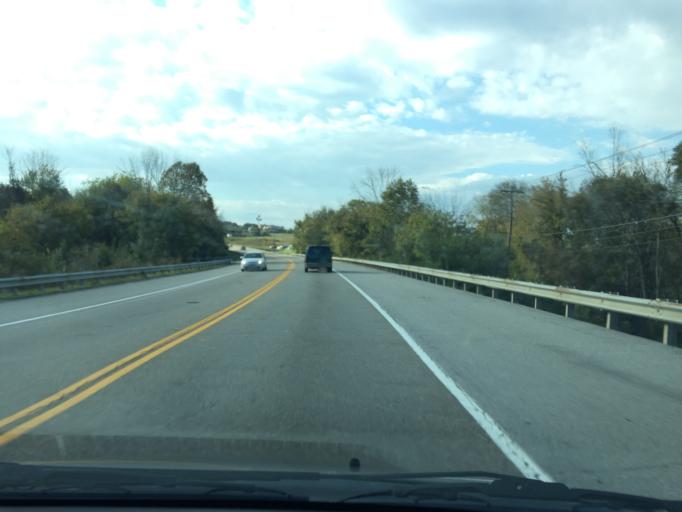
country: US
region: Tennessee
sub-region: Loudon County
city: Loudon
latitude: 35.7289
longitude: -84.3813
